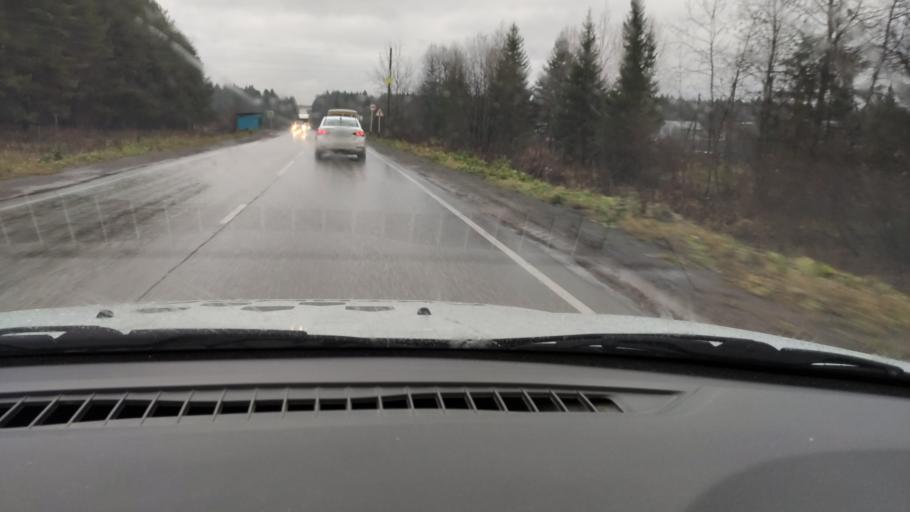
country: RU
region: Perm
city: Novyye Lyady
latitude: 58.0256
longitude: 56.6740
